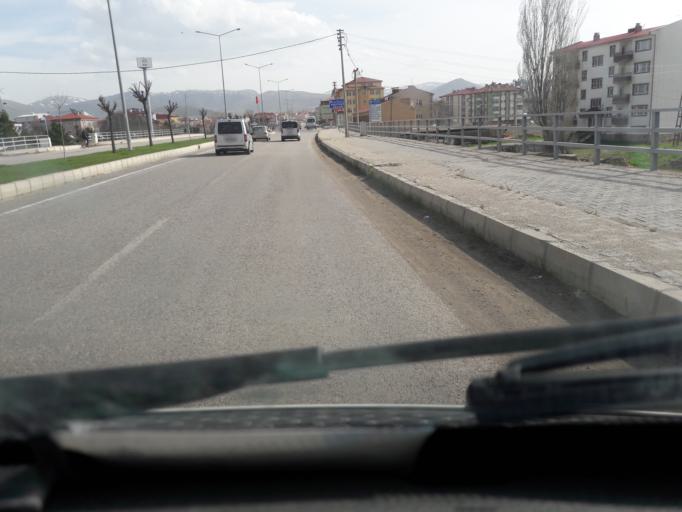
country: TR
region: Gumushane
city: Kelkit
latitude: 40.1386
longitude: 39.4335
